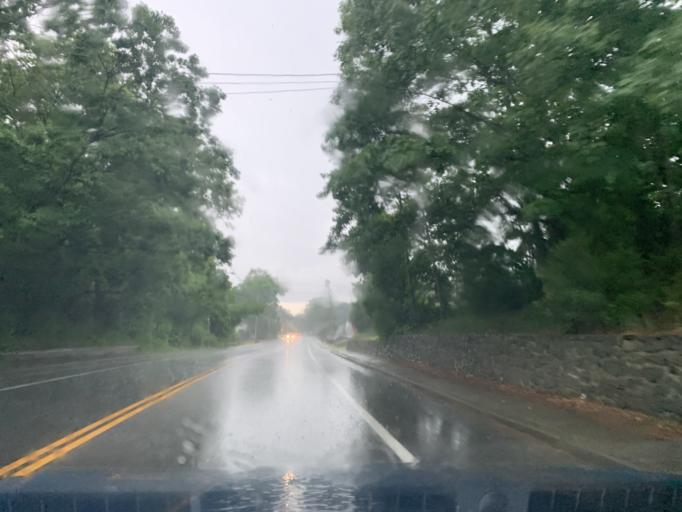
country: US
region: Rhode Island
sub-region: Kent County
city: West Warwick
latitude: 41.7005
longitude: -71.5577
